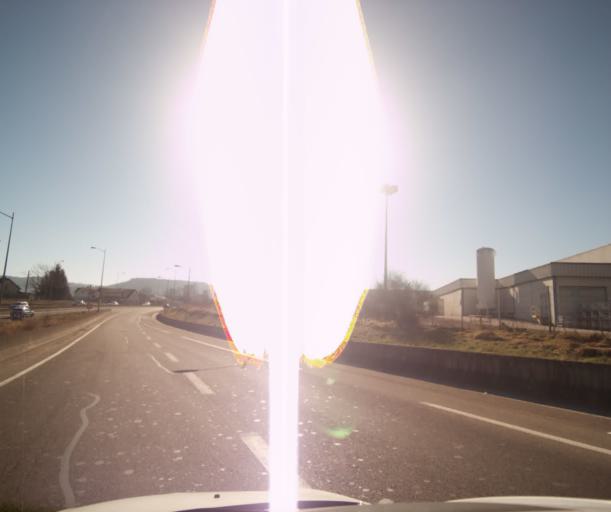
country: FR
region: Franche-Comte
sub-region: Departement du Doubs
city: Pirey
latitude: 47.2325
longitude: 5.9824
